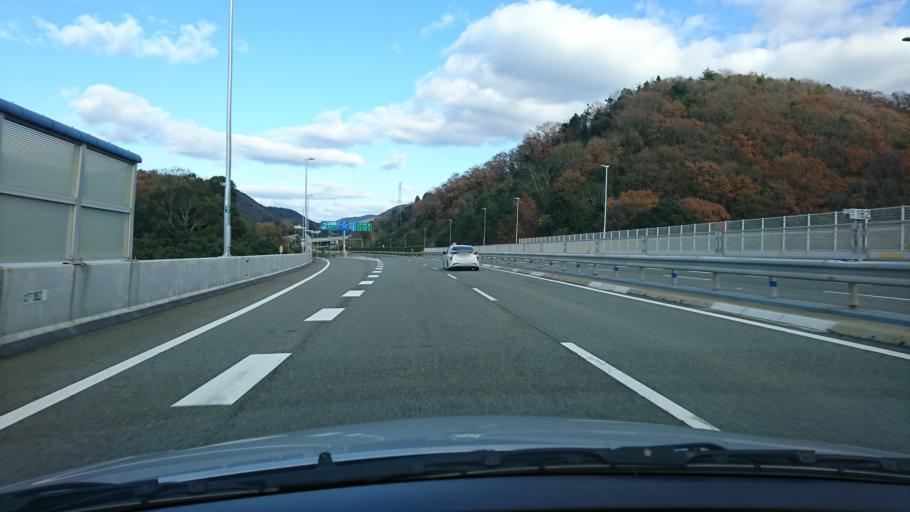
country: JP
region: Hyogo
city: Kobe
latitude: 34.7558
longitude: 135.1552
